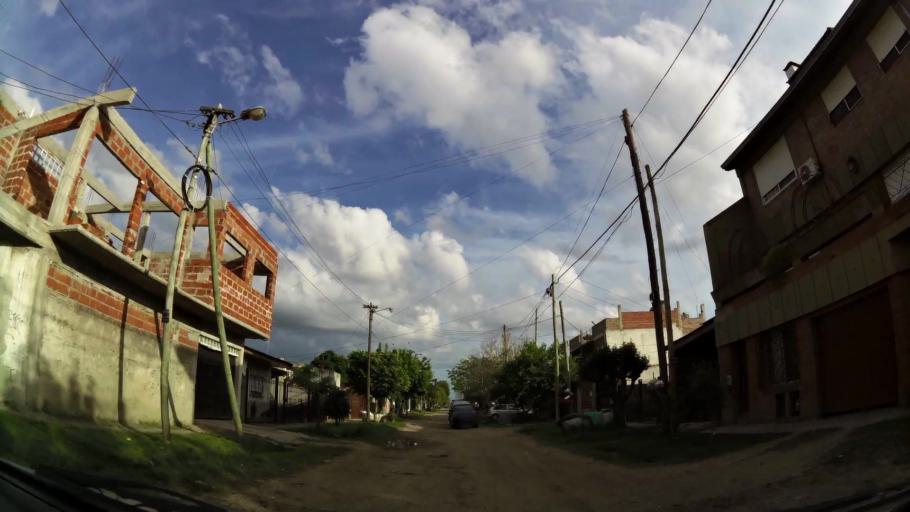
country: AR
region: Buenos Aires
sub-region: Partido de Quilmes
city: Quilmes
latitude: -34.7472
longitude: -58.2569
